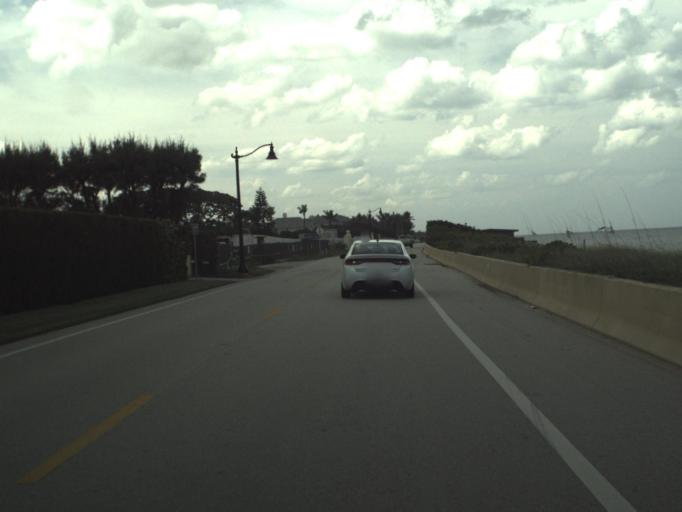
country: US
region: Florida
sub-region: Palm Beach County
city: Lake Worth
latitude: 26.6491
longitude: -80.0372
